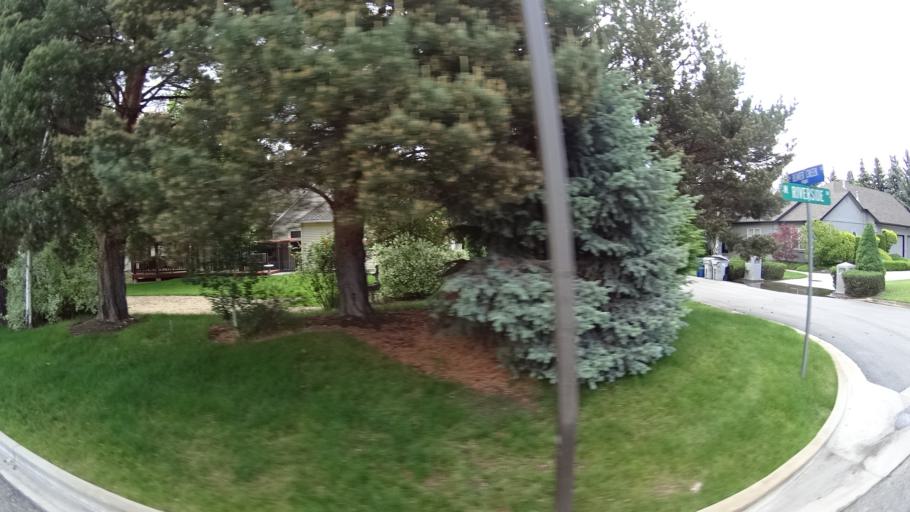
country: US
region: Idaho
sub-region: Ada County
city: Eagle
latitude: 43.6715
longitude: -116.2968
